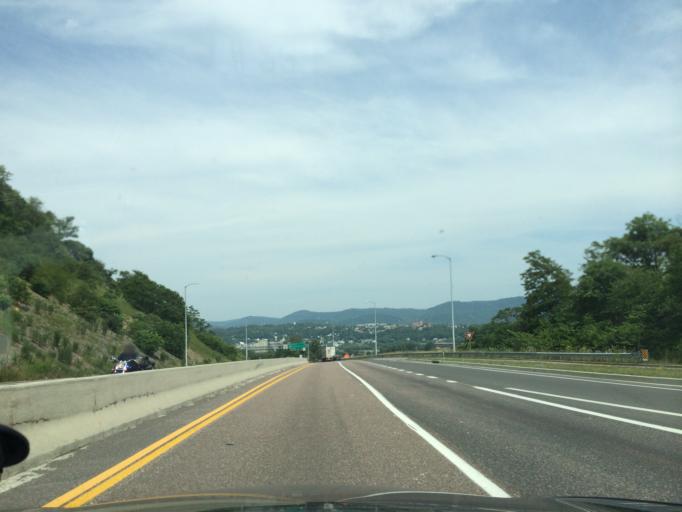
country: US
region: Maryland
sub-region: Allegany County
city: Cumberland
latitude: 39.6452
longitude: -78.7857
